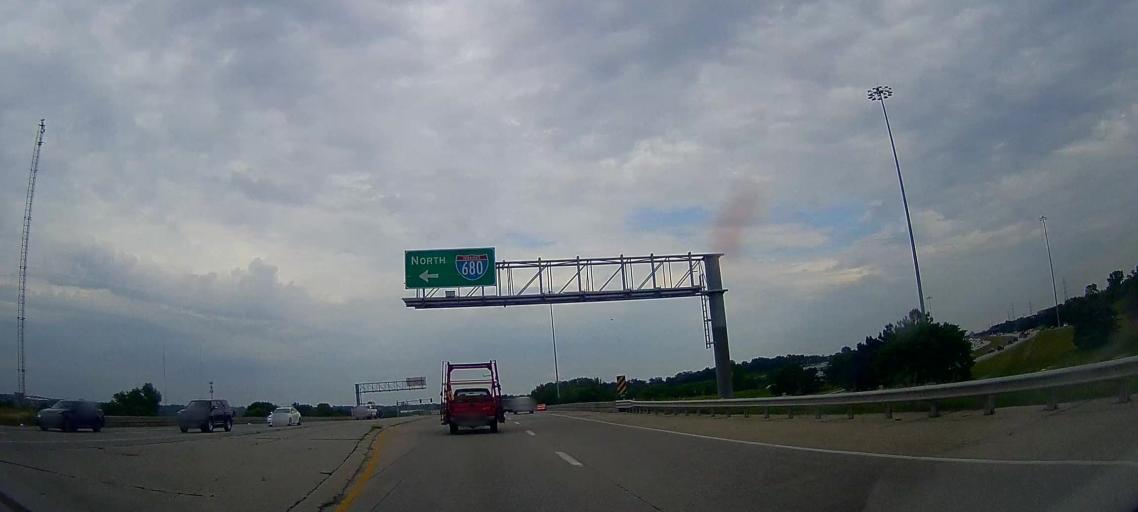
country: US
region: Nebraska
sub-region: Douglas County
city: Bennington
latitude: 41.3227
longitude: -96.0697
